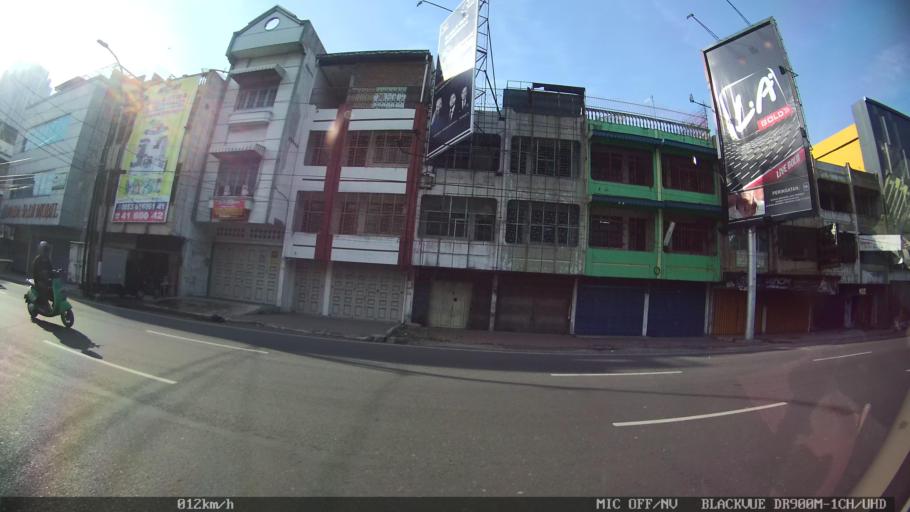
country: ID
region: North Sumatra
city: Medan
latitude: 3.5936
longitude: 98.6708
